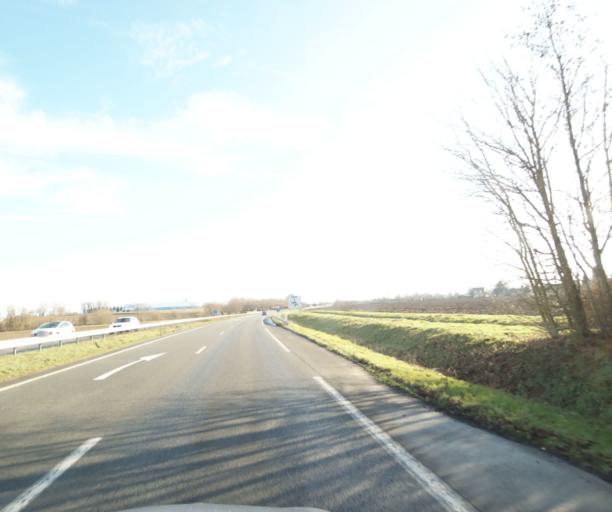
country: FR
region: Nord-Pas-de-Calais
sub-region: Departement du Nord
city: Saultain
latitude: 50.3441
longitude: 3.5805
